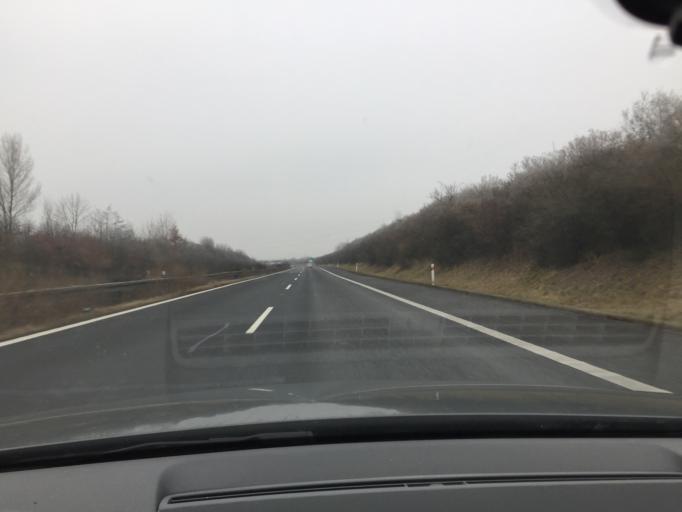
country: CZ
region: Ustecky
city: Lovosice
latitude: 50.4887
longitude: 14.0763
